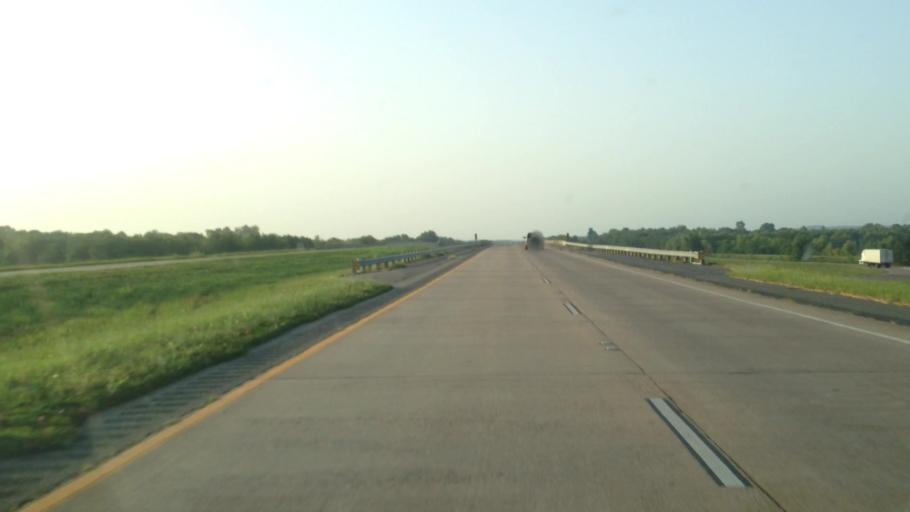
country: US
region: Louisiana
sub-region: Natchitoches Parish
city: Vienna Bend
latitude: 31.6107
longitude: -93.0512
